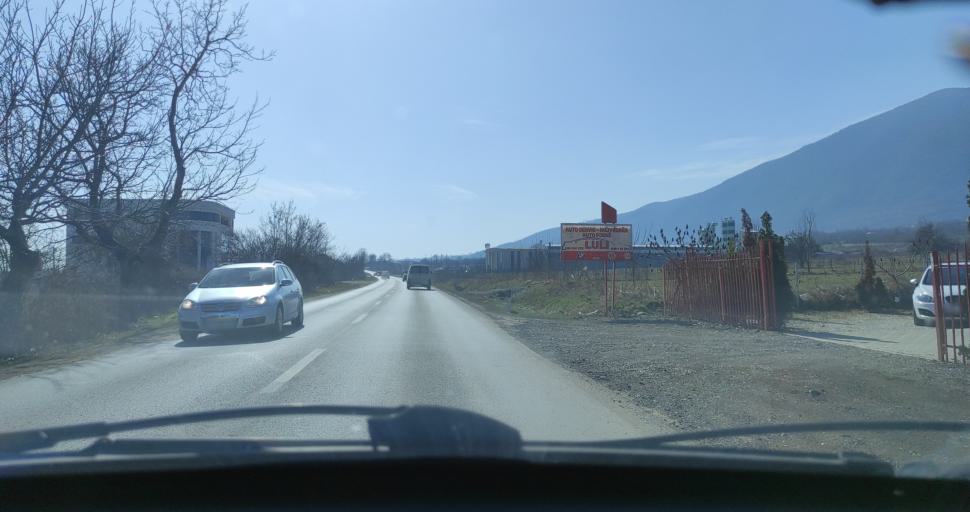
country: XK
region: Gjakova
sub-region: Komuna e Decanit
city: Strellc i Ulet
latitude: 42.6121
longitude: 20.3024
